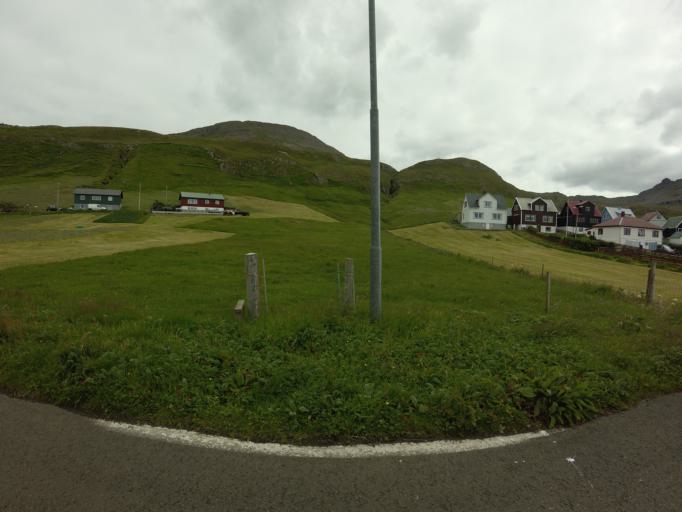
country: FO
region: Suduroy
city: Tvoroyri
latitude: 61.5246
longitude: -6.8794
